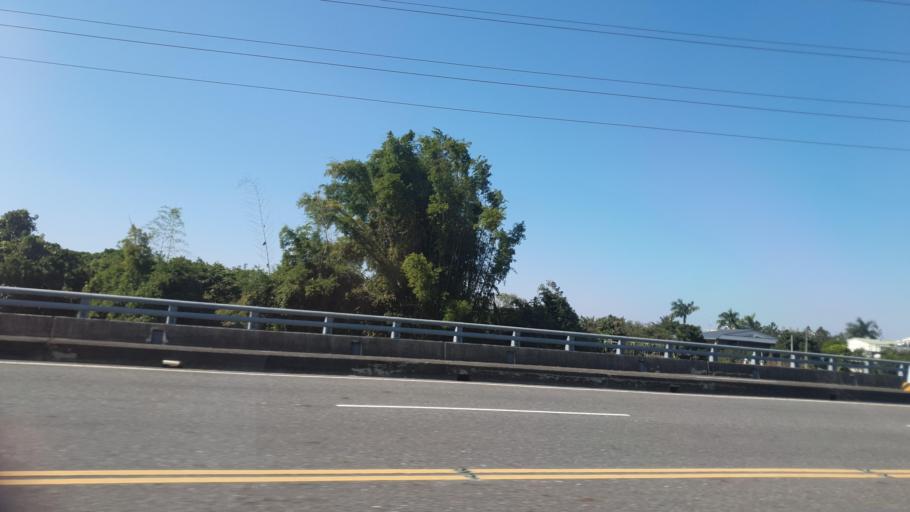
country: TW
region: Taiwan
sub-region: Tainan
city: Tainan
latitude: 23.0346
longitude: 120.3223
